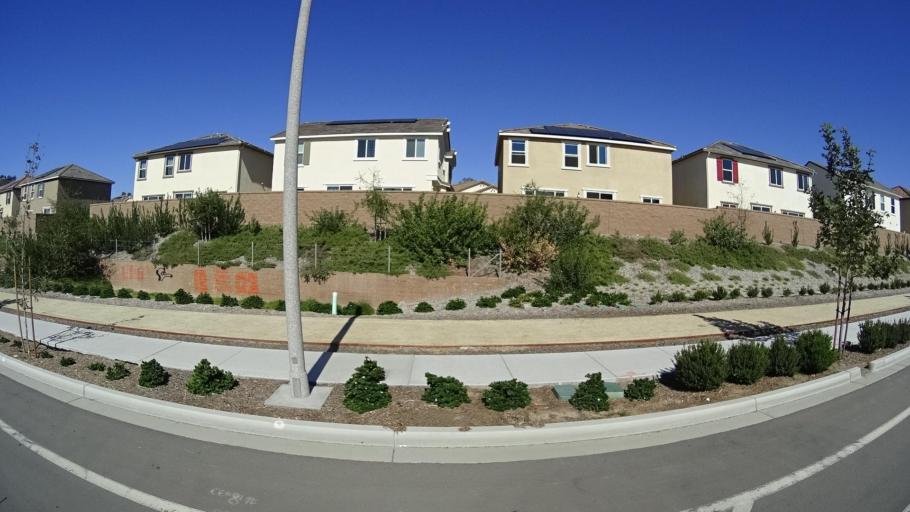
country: US
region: California
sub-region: San Diego County
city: La Presa
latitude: 32.7270
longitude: -116.9671
